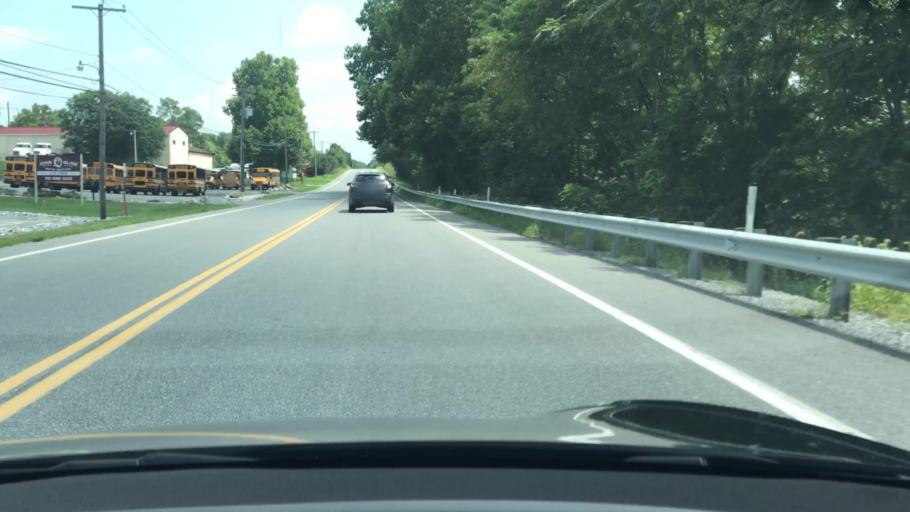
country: US
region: Pennsylvania
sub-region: Lancaster County
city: Salunga
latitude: 40.1051
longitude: -76.4442
